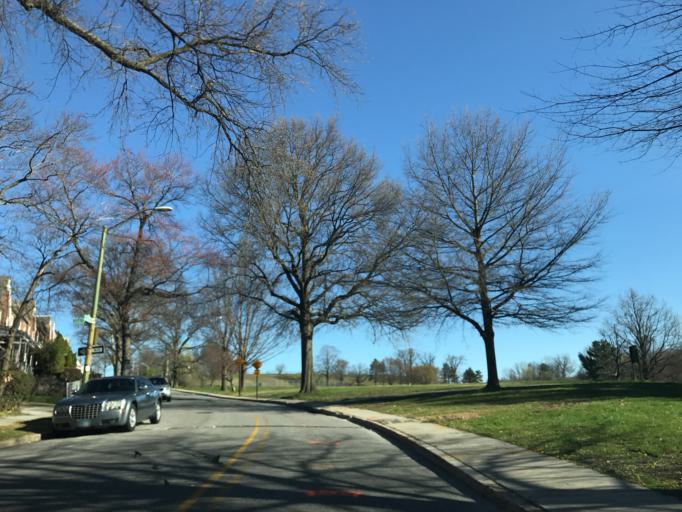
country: US
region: Maryland
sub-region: Baltimore County
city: Lochearn
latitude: 39.3158
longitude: -76.6679
